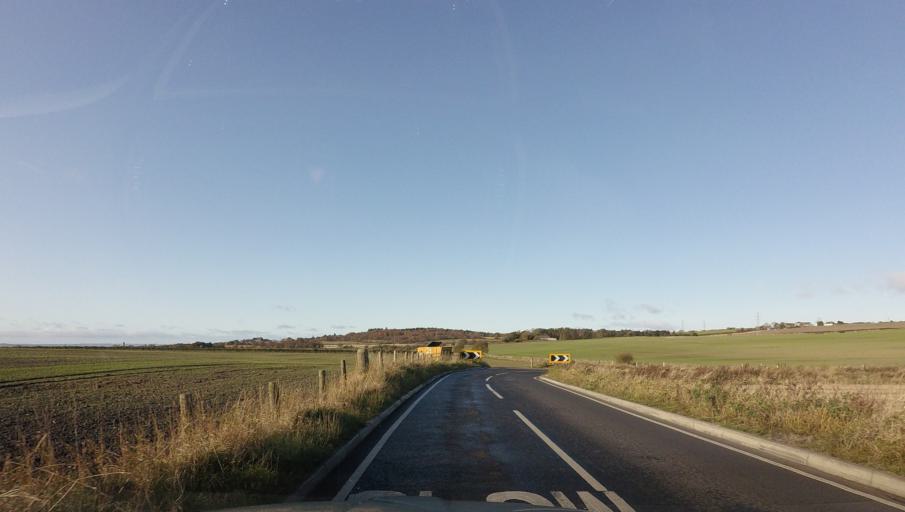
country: GB
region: Scotland
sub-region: Fife
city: Townhill
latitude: 56.0904
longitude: -3.4068
